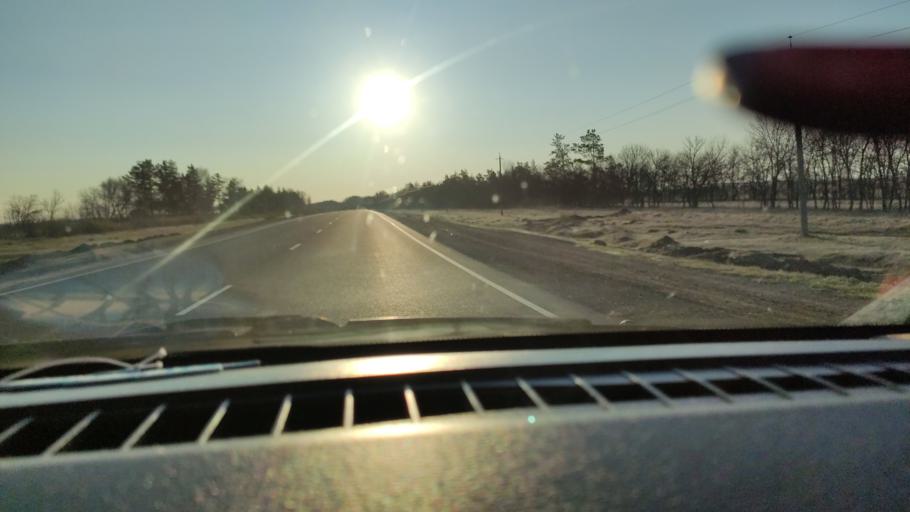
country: RU
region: Saratov
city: Sennoy
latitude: 52.1506
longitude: 46.9896
